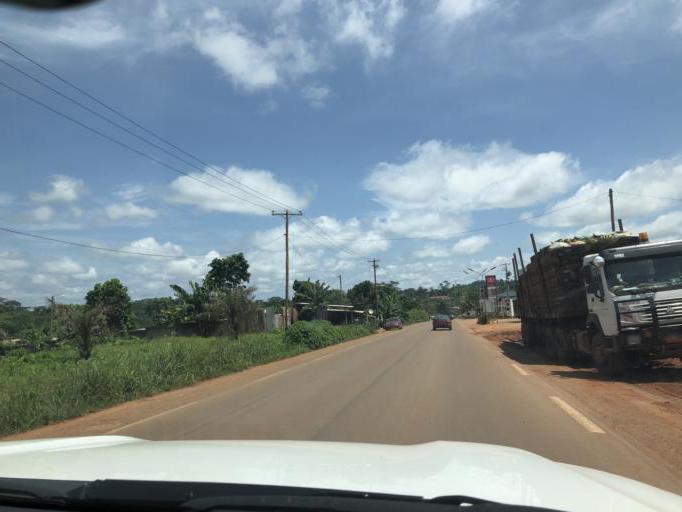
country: CM
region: Centre
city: Yaounde
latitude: 3.8648
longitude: 11.6118
